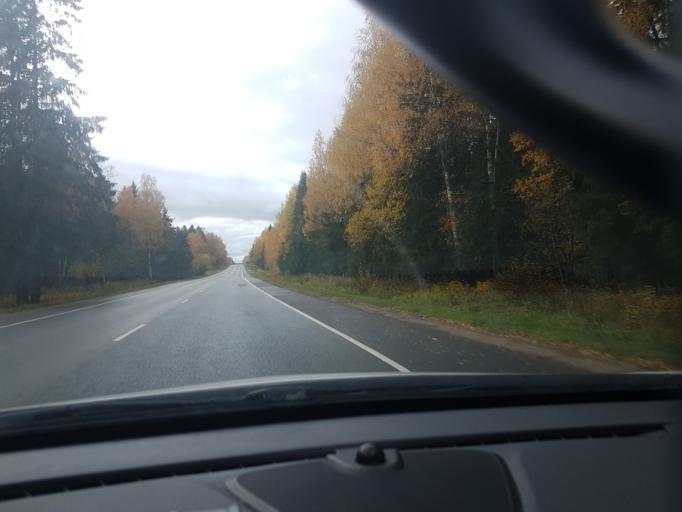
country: RU
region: Moskovskaya
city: Sychevo
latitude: 56.0047
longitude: 36.2879
